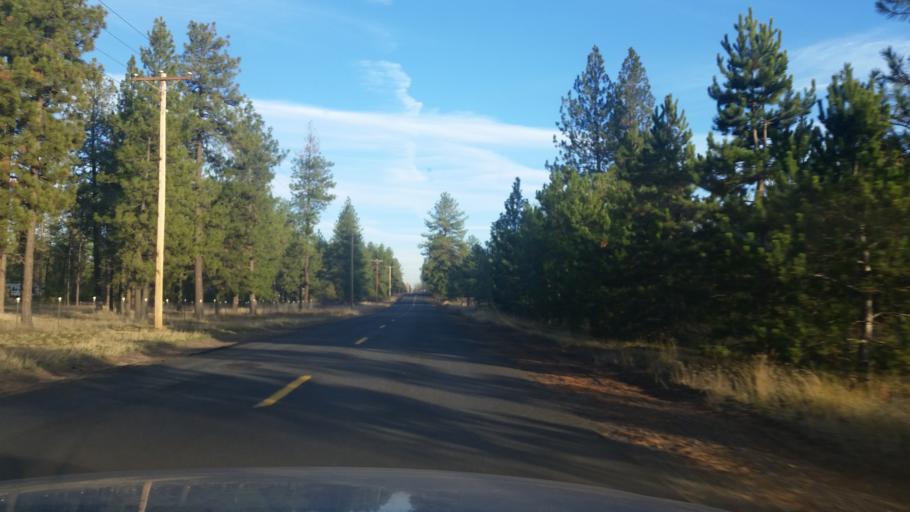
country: US
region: Washington
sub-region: Spokane County
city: Cheney
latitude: 47.5150
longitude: -117.4622
